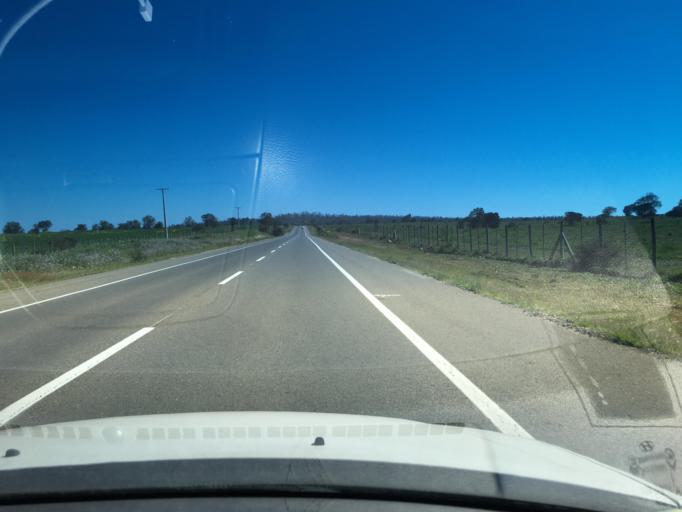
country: CL
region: Valparaiso
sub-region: San Antonio Province
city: El Tabo
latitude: -33.4066
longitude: -71.5371
